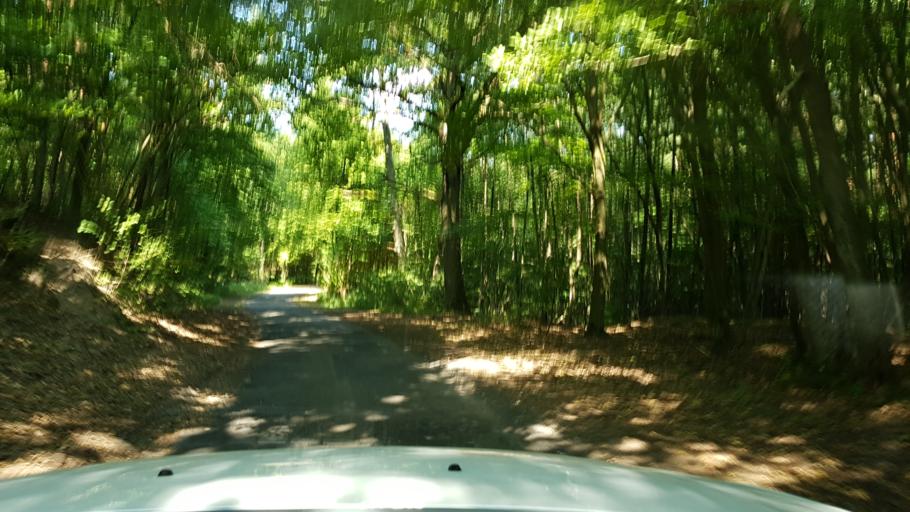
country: DE
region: Brandenburg
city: Neulewin
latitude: 52.8063
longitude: 14.3161
